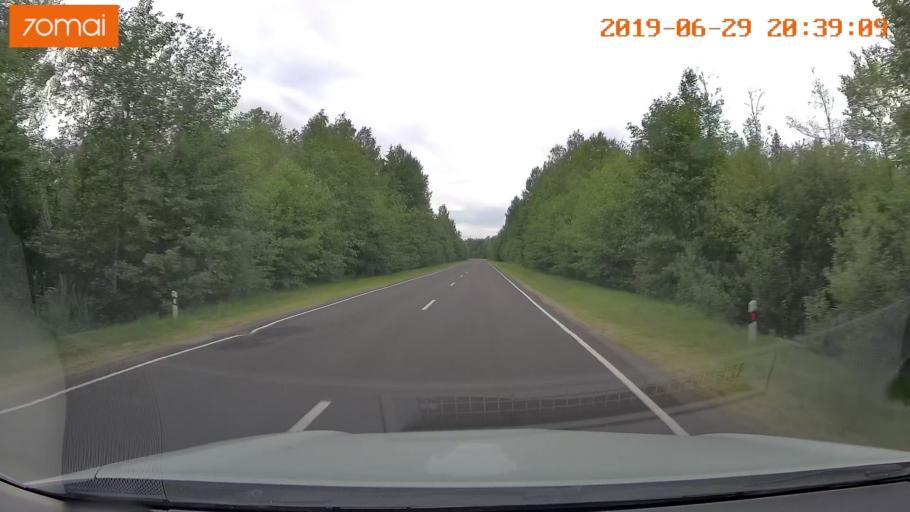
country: BY
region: Brest
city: Hantsavichy
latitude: 52.5587
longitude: 26.3633
